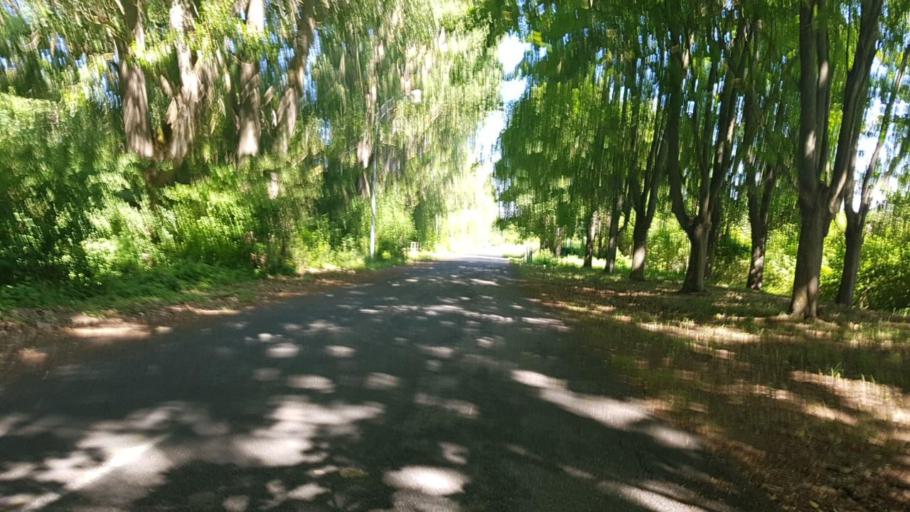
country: FR
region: Ile-de-France
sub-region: Departement de Seine-et-Marne
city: Annet-sur-Marne
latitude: 48.9177
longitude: 2.7293
